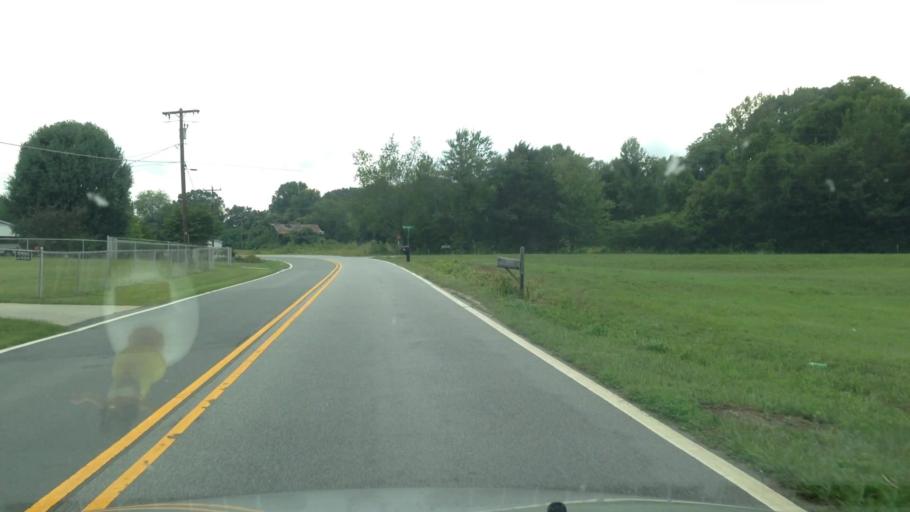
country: US
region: North Carolina
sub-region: Forsyth County
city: Walkertown
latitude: 36.1584
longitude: -80.1112
